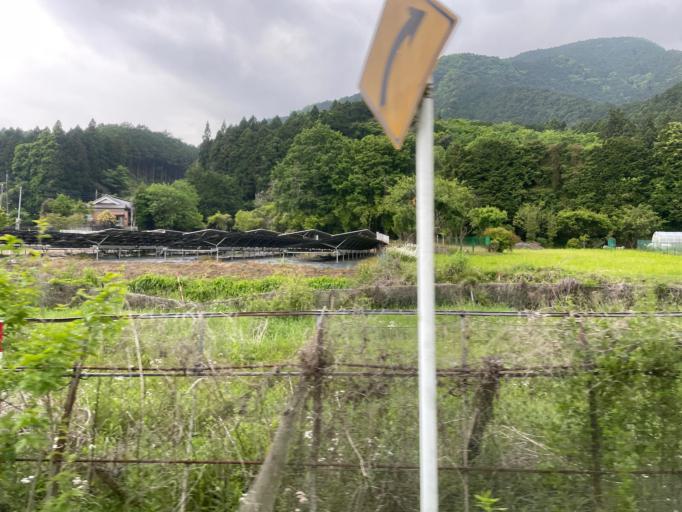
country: JP
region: Tochigi
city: Tanuma
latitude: 36.4594
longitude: 139.6363
